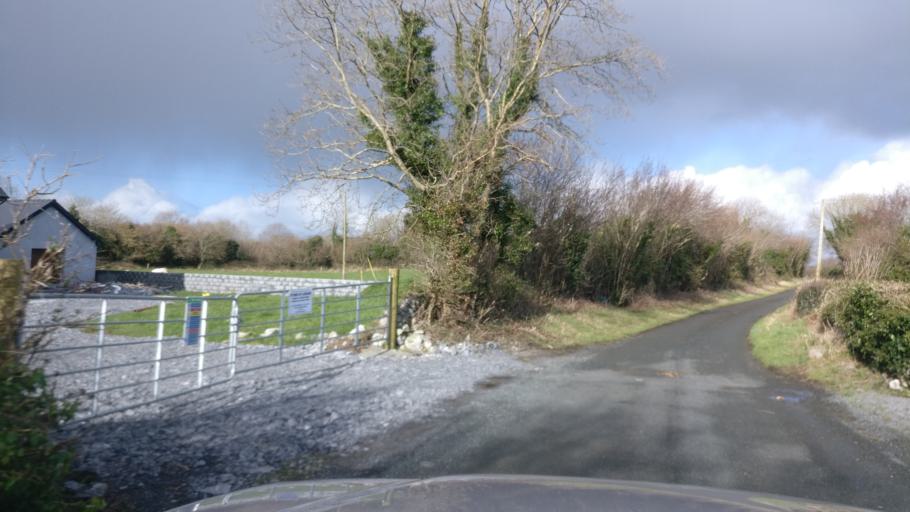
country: IE
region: Connaught
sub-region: County Galway
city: Oranmore
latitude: 53.2381
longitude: -8.8316
